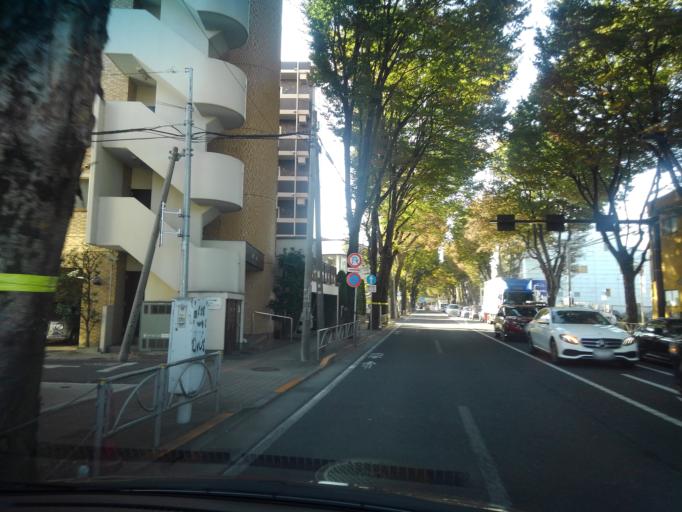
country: JP
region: Tokyo
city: Chofugaoka
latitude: 35.6527
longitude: 139.5566
